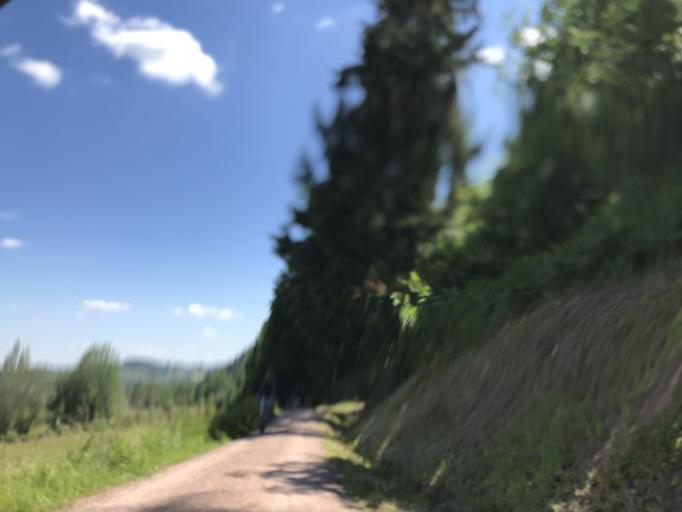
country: DE
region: Baden-Wuerttemberg
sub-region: Freiburg Region
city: Hausen
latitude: 47.6760
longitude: 7.8302
